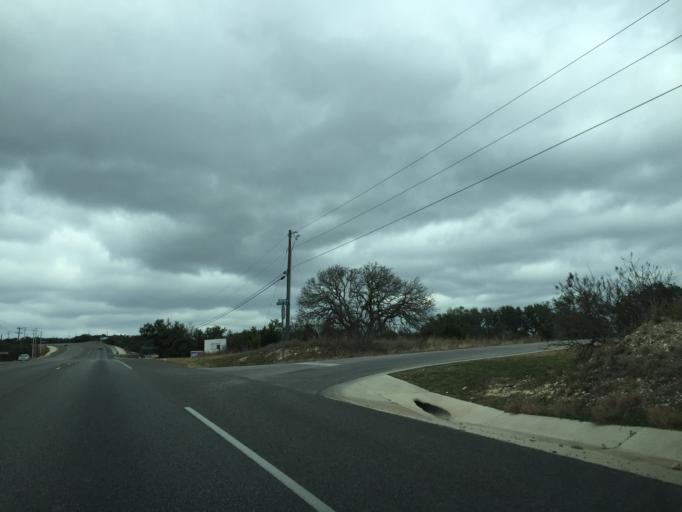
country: US
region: Texas
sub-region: Travis County
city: The Hills
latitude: 30.3437
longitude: -98.0463
